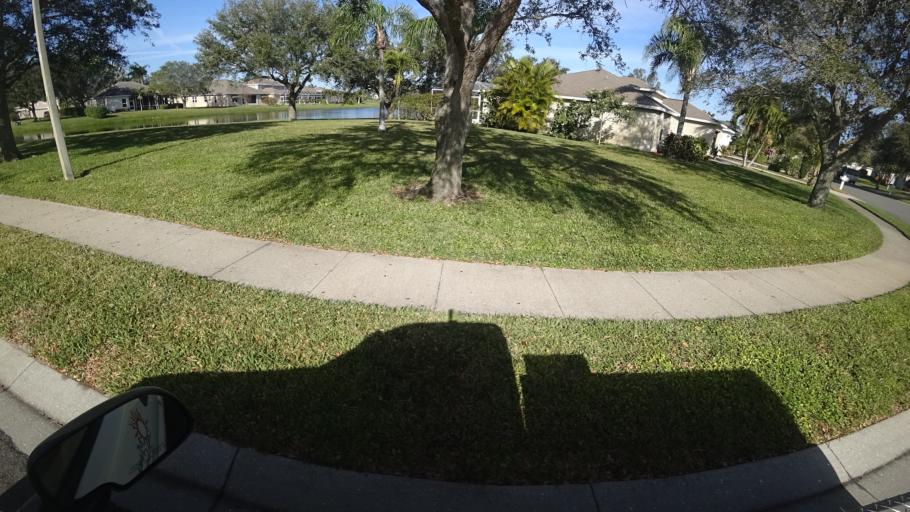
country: US
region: Florida
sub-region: Manatee County
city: Bayshore Gardens
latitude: 27.4492
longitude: -82.6155
